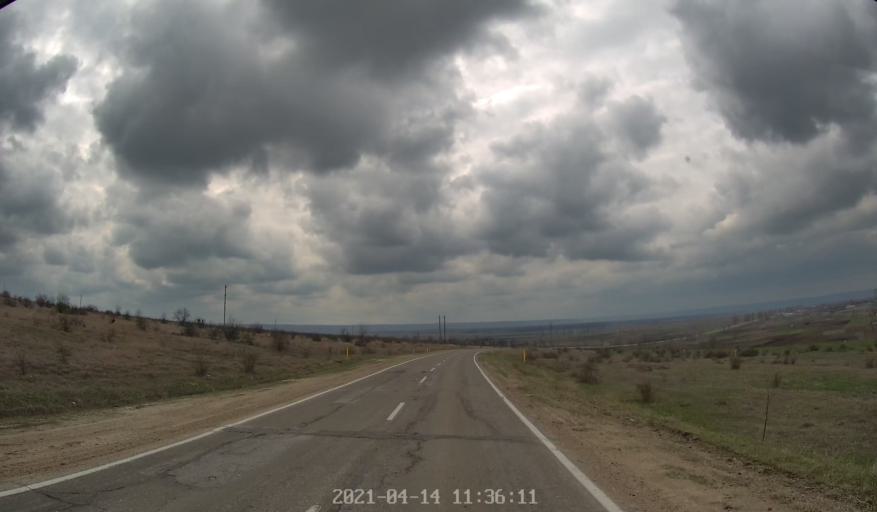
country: MD
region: Criuleni
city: Criuleni
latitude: 47.1624
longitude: 29.1634
